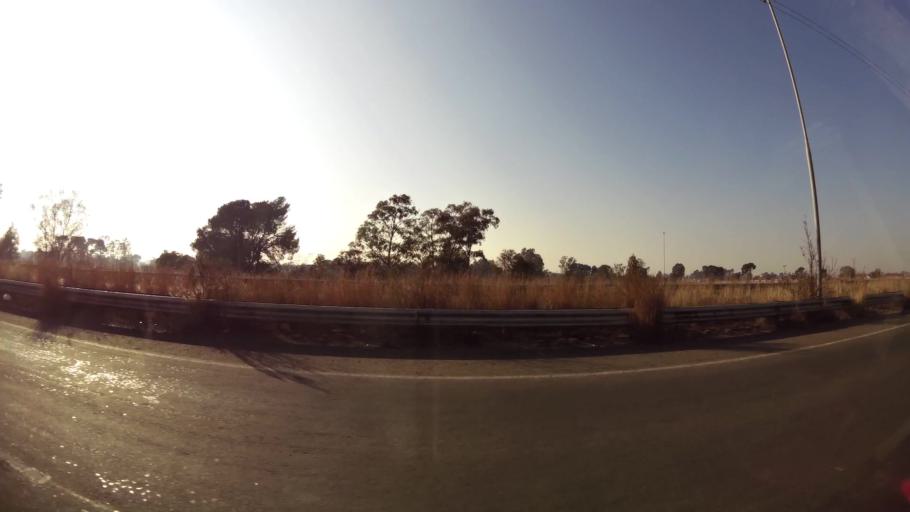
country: ZA
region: Orange Free State
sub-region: Mangaung Metropolitan Municipality
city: Bloemfontein
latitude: -29.1356
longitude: 26.2672
